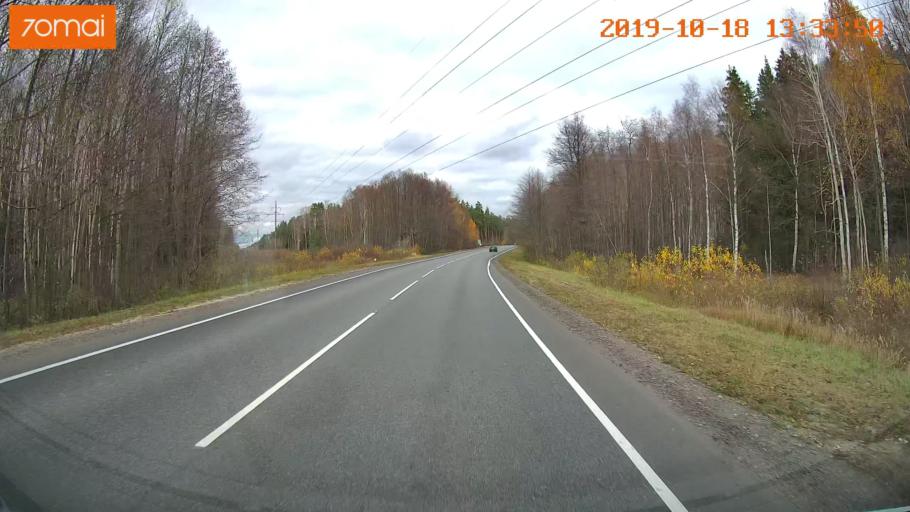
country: RU
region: Rjazan
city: Solotcha
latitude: 54.8483
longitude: 39.9429
